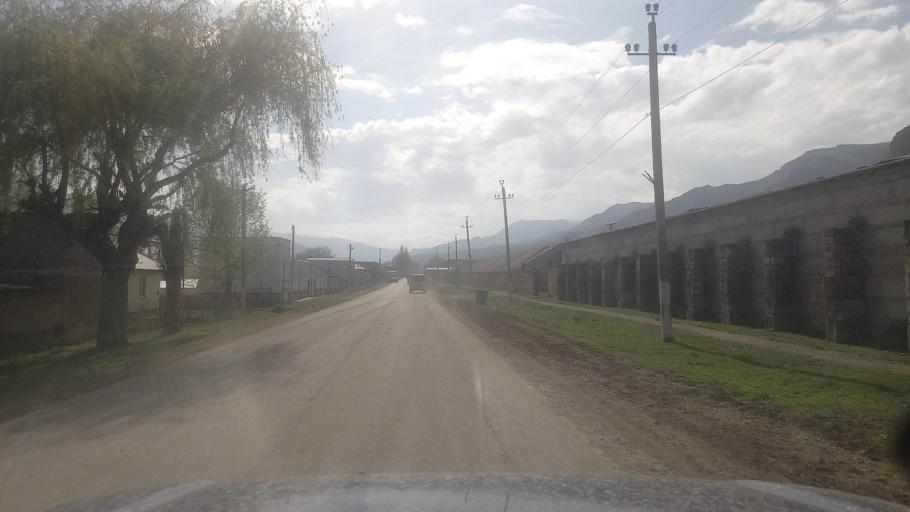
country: RU
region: Kabardino-Balkariya
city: Kamennomostskoye
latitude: 43.7319
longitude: 42.9541
